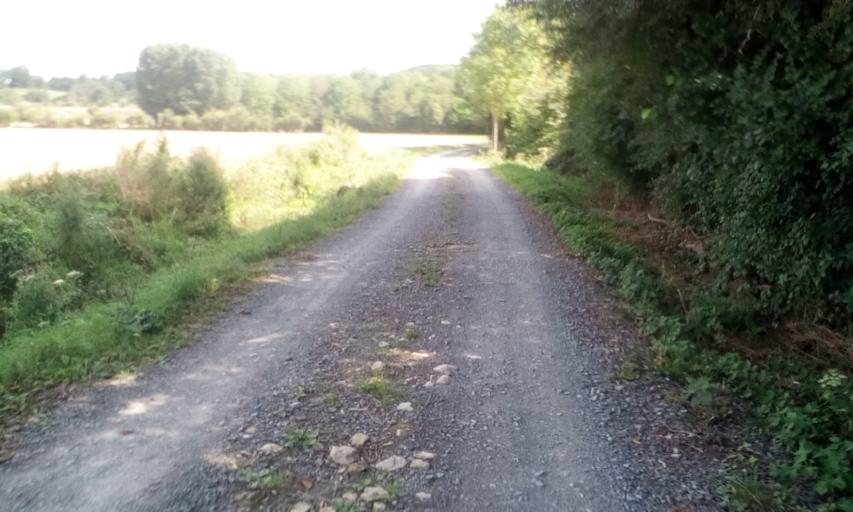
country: FR
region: Lower Normandy
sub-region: Departement du Calvados
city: Argences
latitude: 49.1418
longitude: -0.1694
